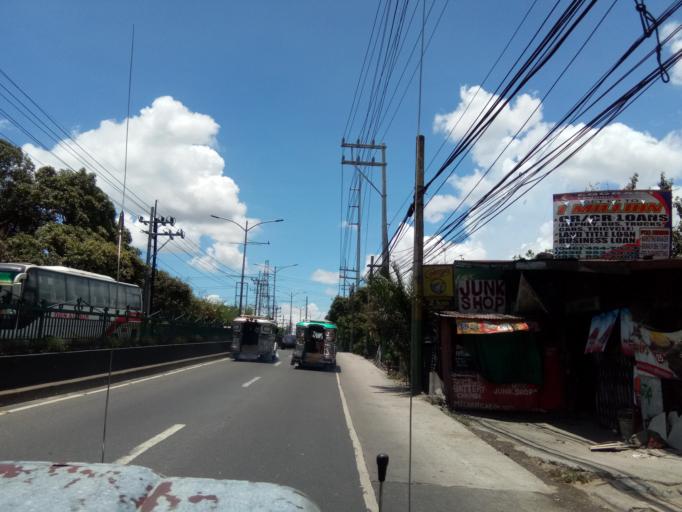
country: PH
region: Calabarzon
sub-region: Province of Cavite
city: Dasmarinas
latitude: 14.3127
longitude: 120.9476
